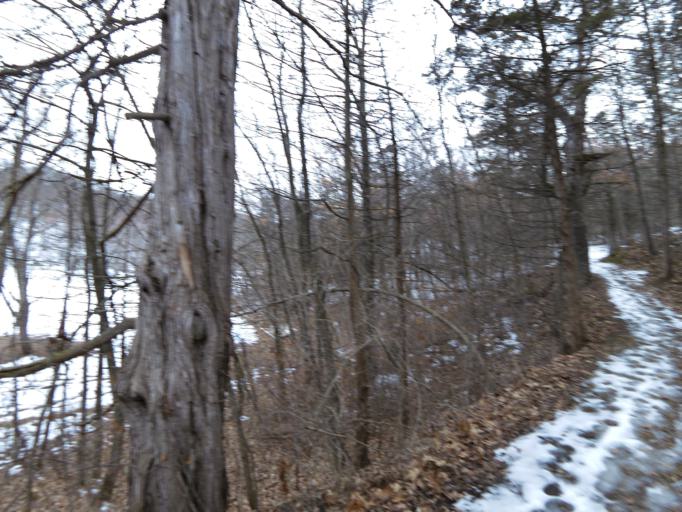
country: US
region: Wisconsin
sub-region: Pierce County
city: Prescott
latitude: 44.7993
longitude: -92.7889
